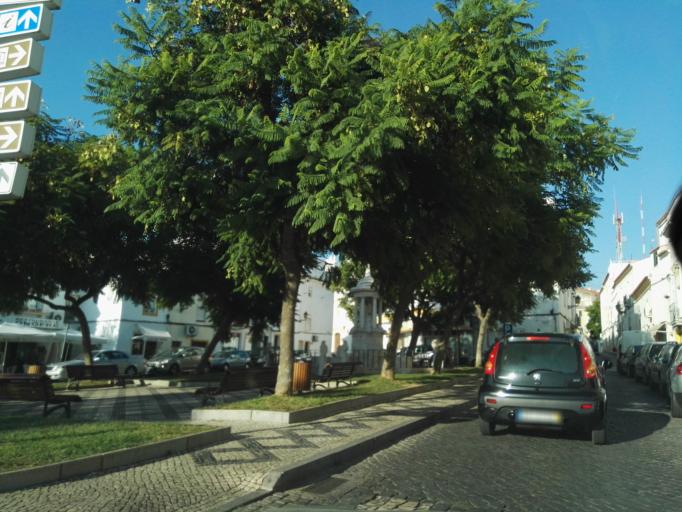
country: PT
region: Portalegre
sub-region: Elvas
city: Elvas
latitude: 38.8787
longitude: -7.1661
